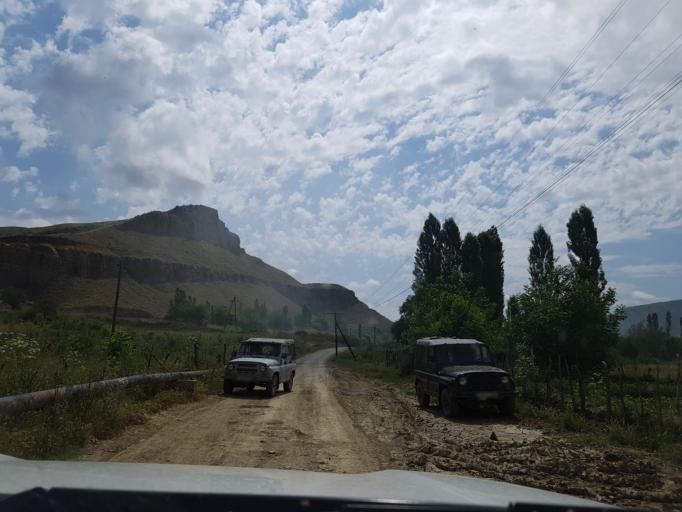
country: TM
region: Ahal
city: Baharly
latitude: 38.2260
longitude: 56.8789
